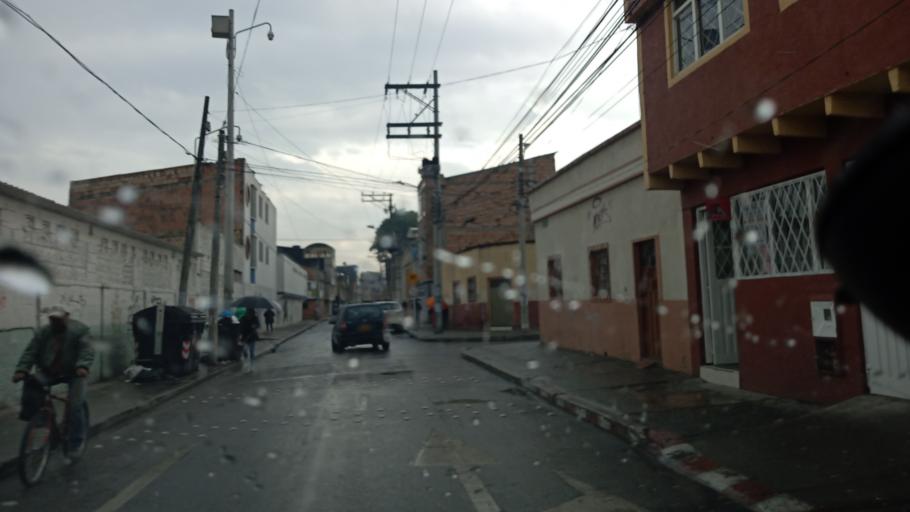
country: CO
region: Cundinamarca
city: Funza
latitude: 4.6788
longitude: -74.1475
